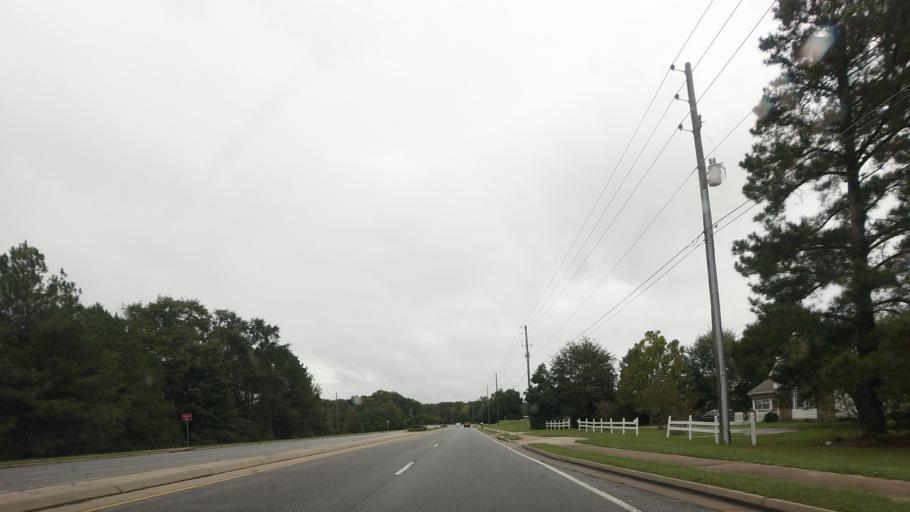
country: US
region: Georgia
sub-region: Houston County
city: Centerville
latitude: 32.5356
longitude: -83.6606
